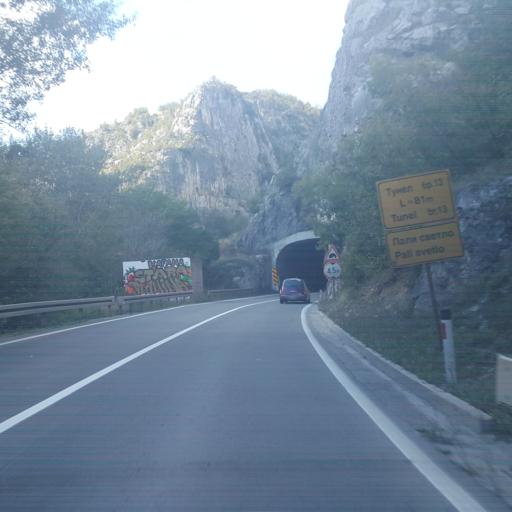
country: RS
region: Central Serbia
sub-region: Nisavski Okrug
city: Svrljig
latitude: 43.3108
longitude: 22.1797
